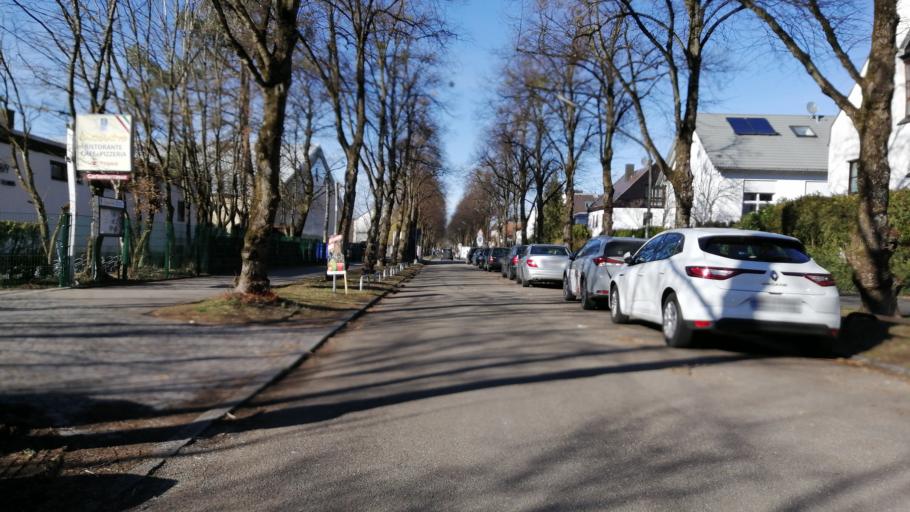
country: DE
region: Bavaria
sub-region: Upper Bavaria
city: Neuried
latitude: 48.1074
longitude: 11.5082
